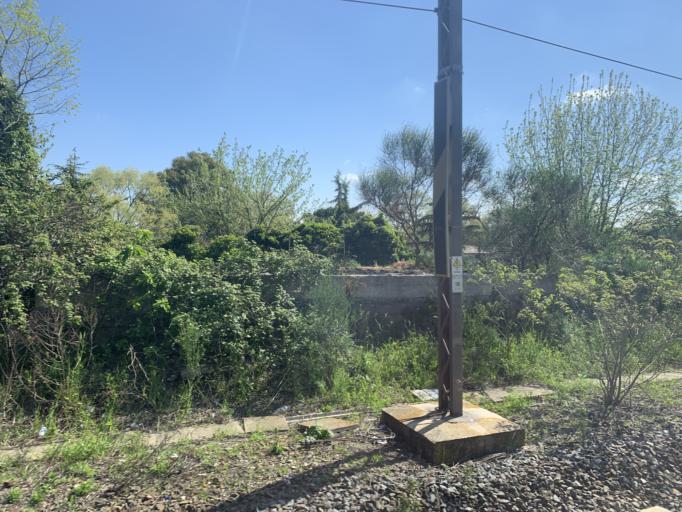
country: IT
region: Latium
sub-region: Citta metropolitana di Roma Capitale
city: Ciampino
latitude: 41.8299
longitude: 12.5695
